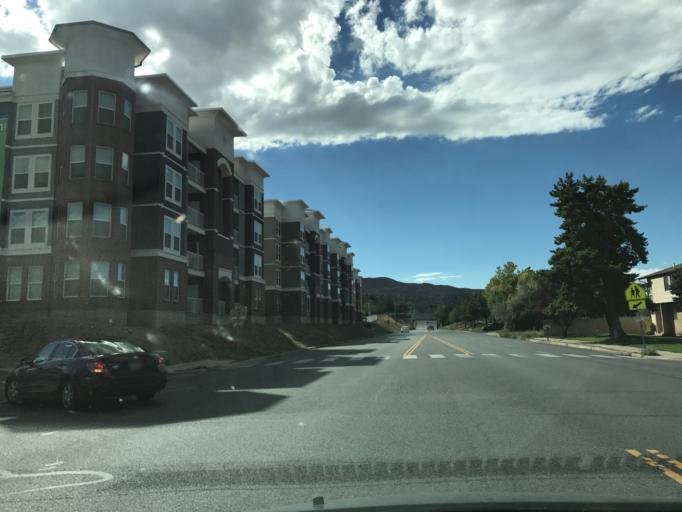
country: US
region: Utah
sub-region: Davis County
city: Woods Cross
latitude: 40.8717
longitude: -111.8922
